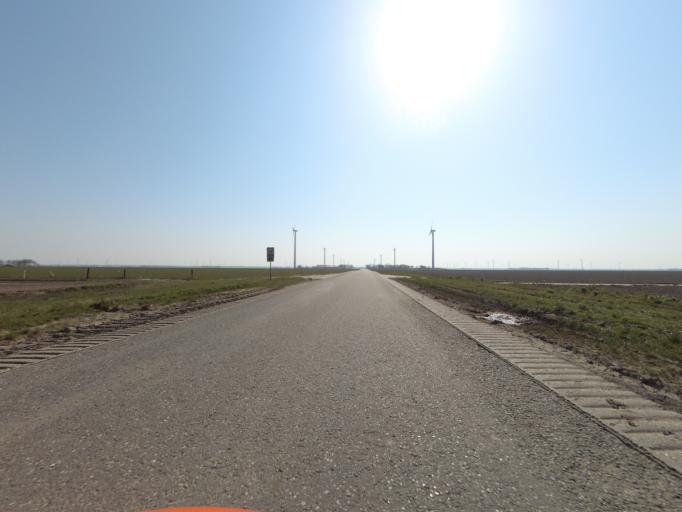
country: NL
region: Utrecht
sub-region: Gemeente Bunschoten
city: Spakenburg
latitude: 52.3499
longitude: 5.3683
